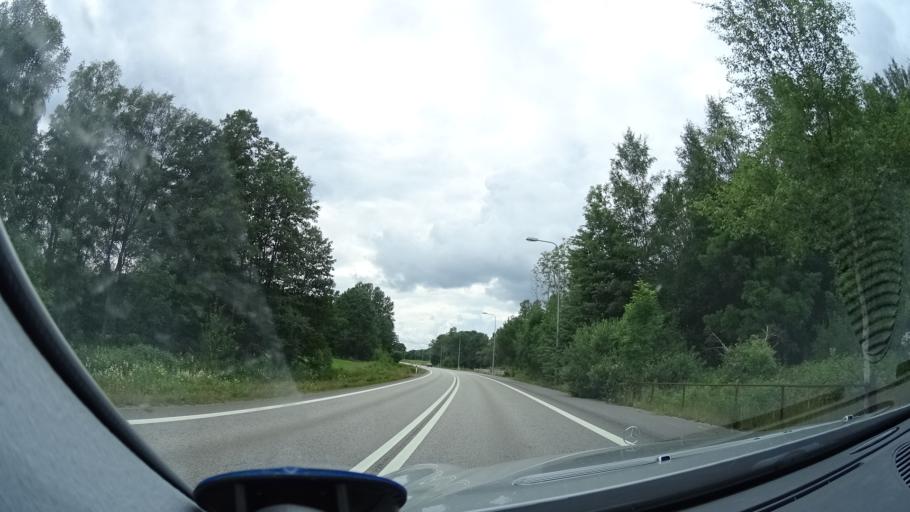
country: SE
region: Kronoberg
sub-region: Tingsryds Kommun
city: Tingsryd
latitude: 56.4986
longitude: 15.0630
